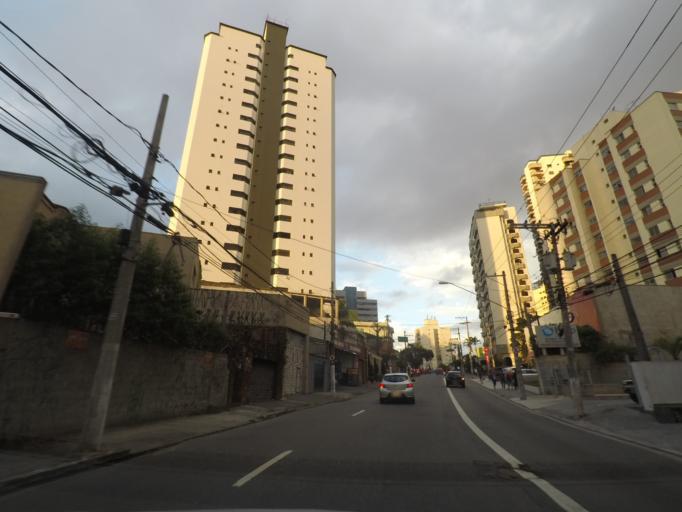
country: BR
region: Sao Paulo
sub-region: Sao Paulo
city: Sao Paulo
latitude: -23.4882
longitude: -46.6233
